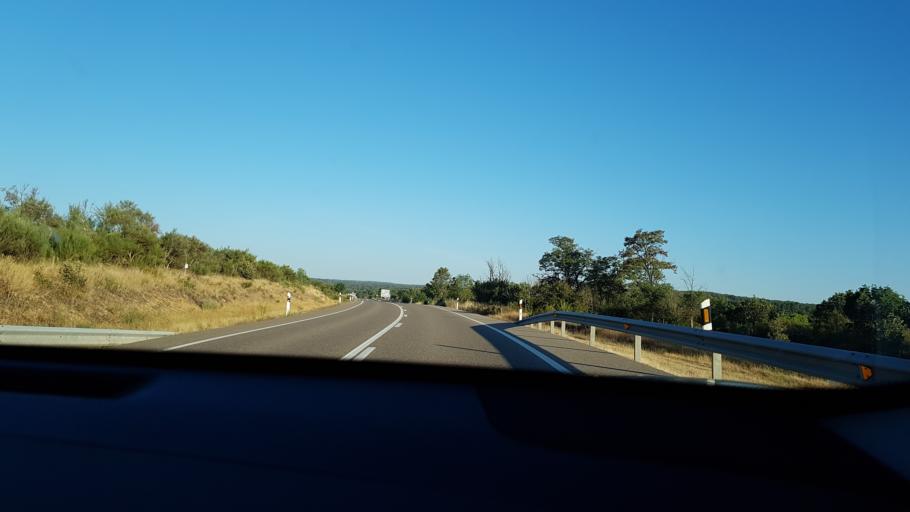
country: ES
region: Castille and Leon
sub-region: Provincia de Zamora
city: Samir de los Canos
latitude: 41.6534
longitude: -6.1790
